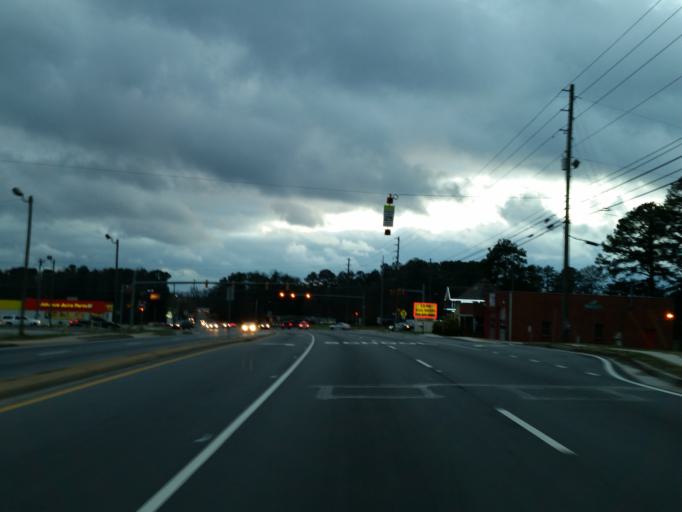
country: US
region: Georgia
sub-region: Cobb County
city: Fair Oaks
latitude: 33.8965
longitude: -84.5756
